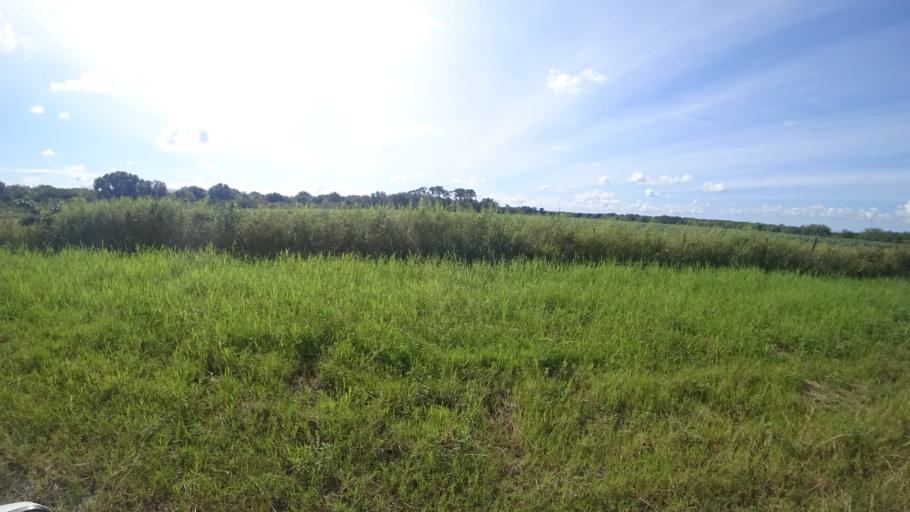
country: US
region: Florida
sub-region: Sarasota County
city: The Meadows
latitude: 27.4440
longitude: -82.3154
